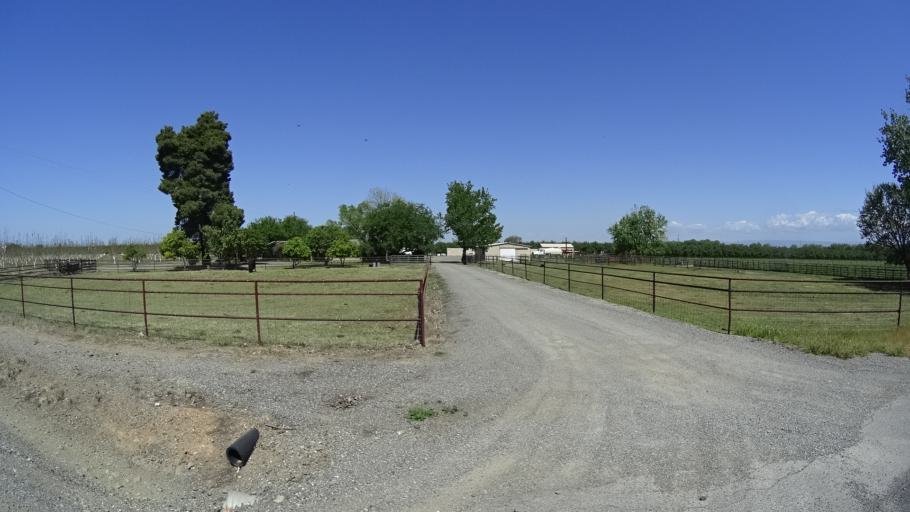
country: US
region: California
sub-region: Glenn County
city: Hamilton City
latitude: 39.7664
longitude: -122.0379
